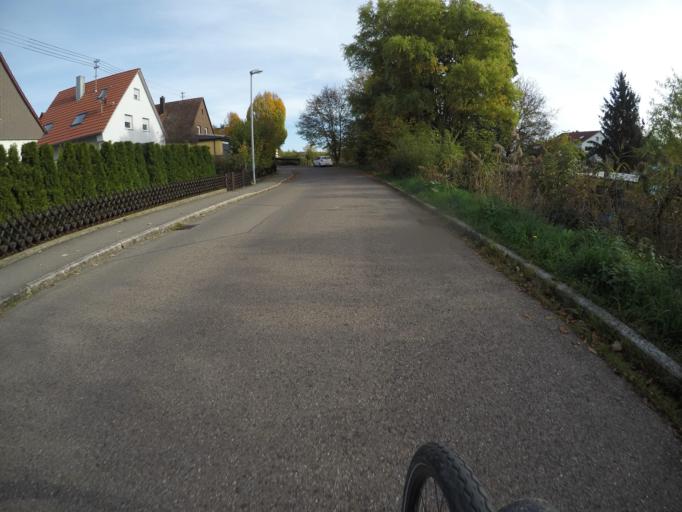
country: DE
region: Baden-Wuerttemberg
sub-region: Regierungsbezirk Stuttgart
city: Magstadt
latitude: 48.7377
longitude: 8.9691
